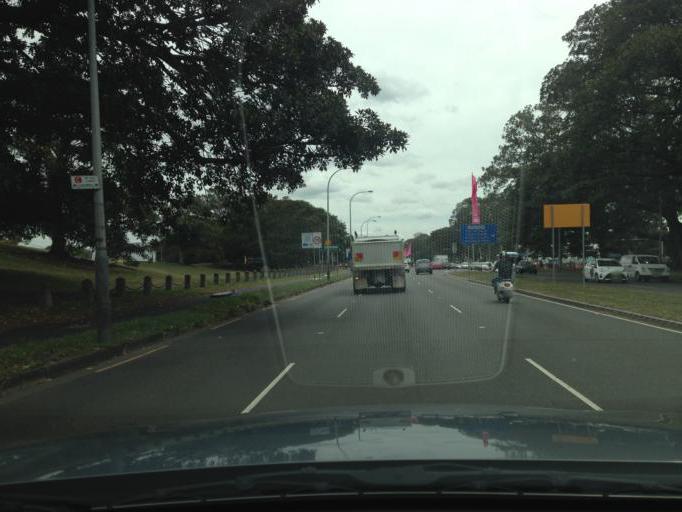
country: AU
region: New South Wales
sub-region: Woollahra
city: Paddington
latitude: -33.8969
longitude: 151.2217
